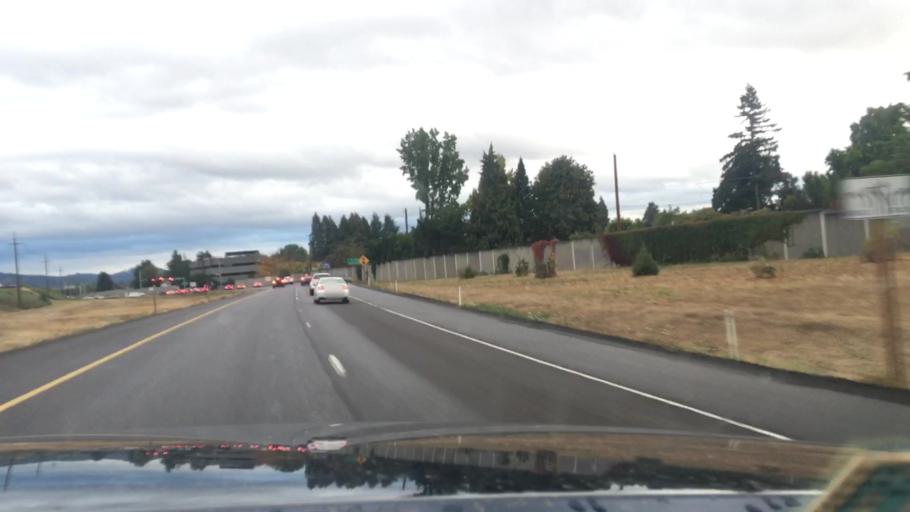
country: US
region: Oregon
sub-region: Lane County
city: Eugene
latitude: 44.0874
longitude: -123.0723
